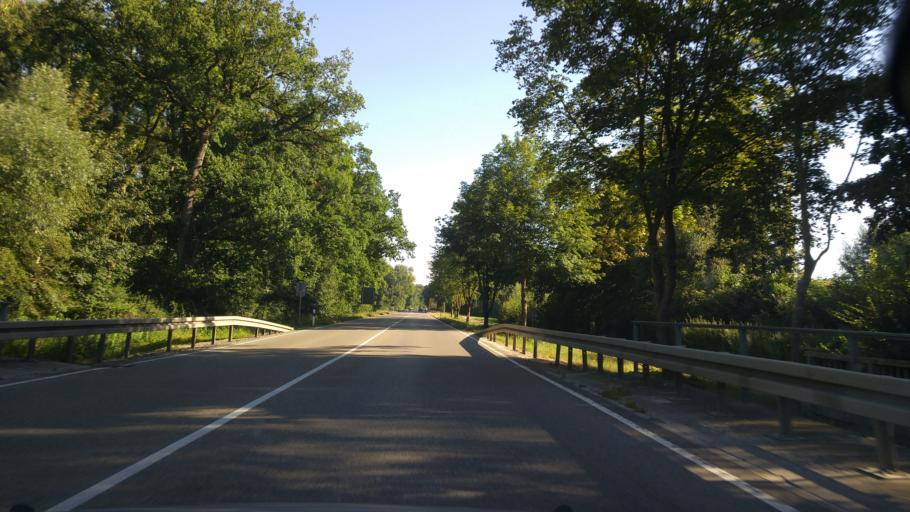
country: DE
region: Bavaria
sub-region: Swabia
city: Guenzburg
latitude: 48.4748
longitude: 10.2837
